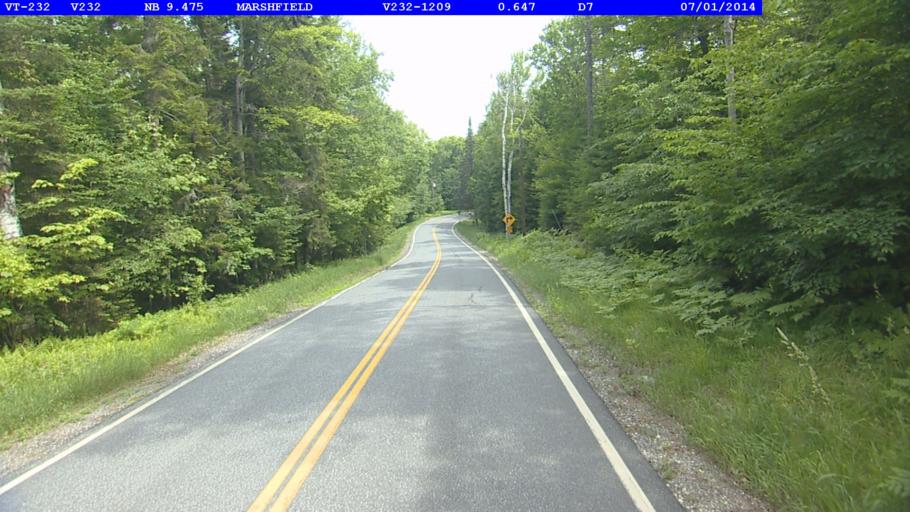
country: US
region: Vermont
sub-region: Caledonia County
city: Hardwick
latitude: 44.3252
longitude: -72.2893
